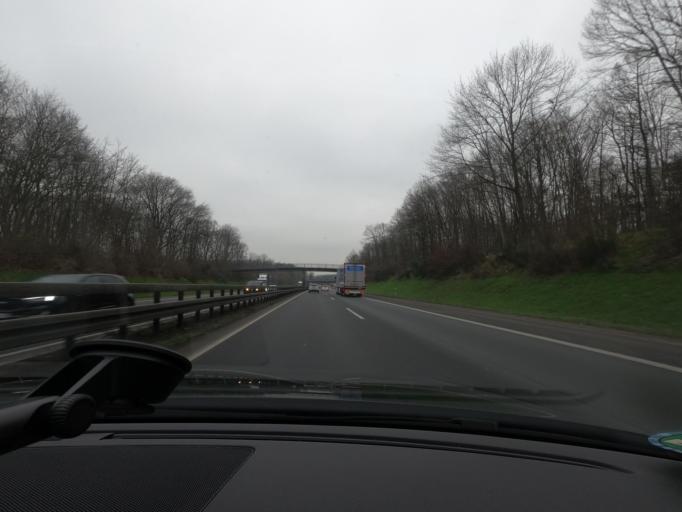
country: DE
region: North Rhine-Westphalia
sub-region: Regierungsbezirk Dusseldorf
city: Viersen
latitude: 51.2199
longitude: 6.3709
